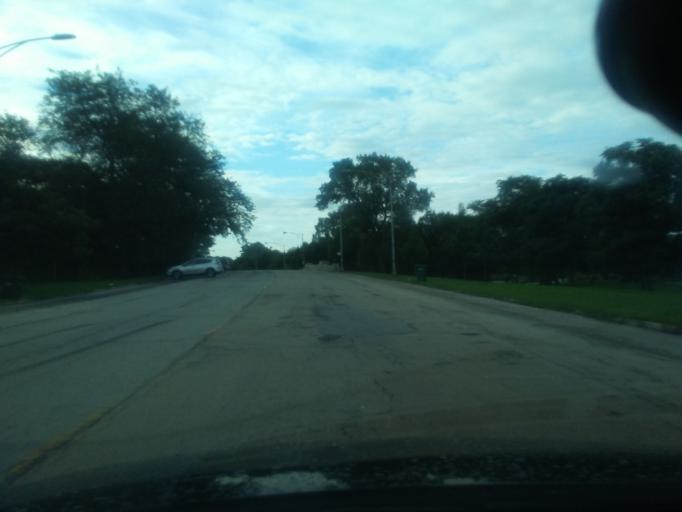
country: US
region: Illinois
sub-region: Cook County
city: Evanston
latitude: 41.9688
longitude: -87.6452
